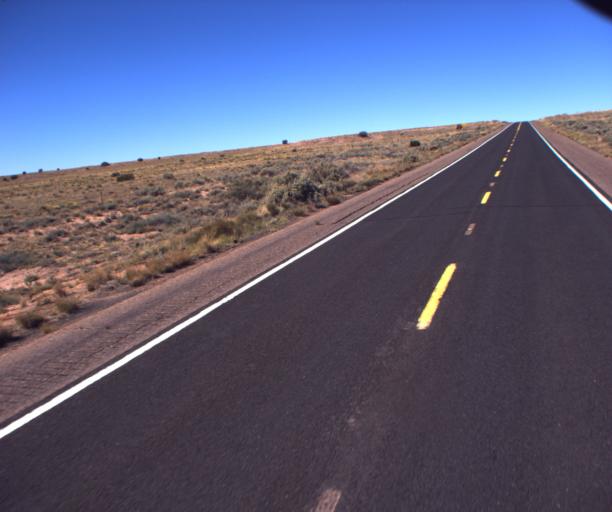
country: US
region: Arizona
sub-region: Navajo County
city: Snowflake
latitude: 34.6988
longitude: -109.7516
